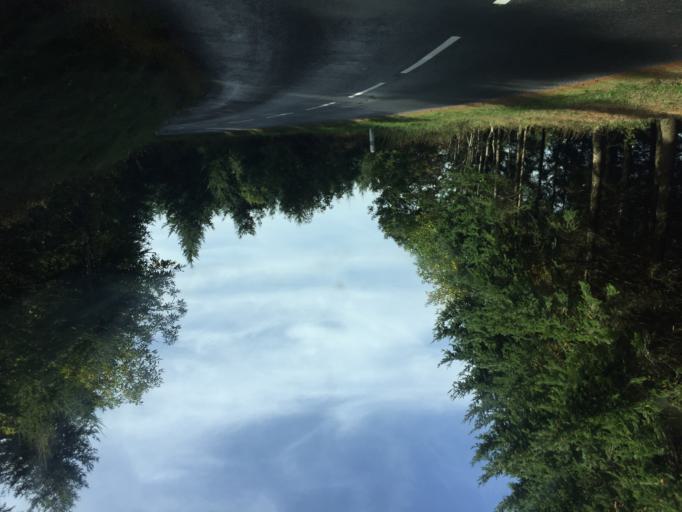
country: FR
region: Rhone-Alpes
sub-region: Departement du Rhone
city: Grandris
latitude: 46.0921
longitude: 4.4502
